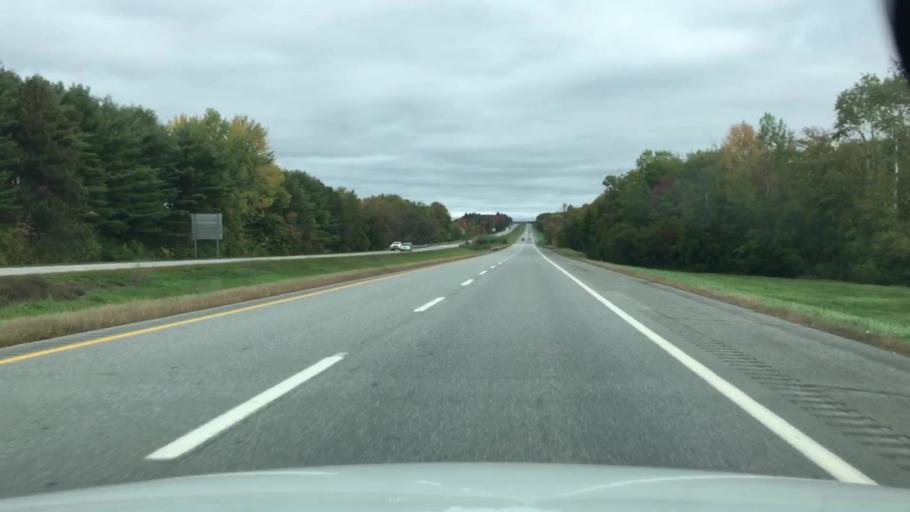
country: US
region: Maine
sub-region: Penobscot County
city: Newport
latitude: 44.8271
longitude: -69.2777
